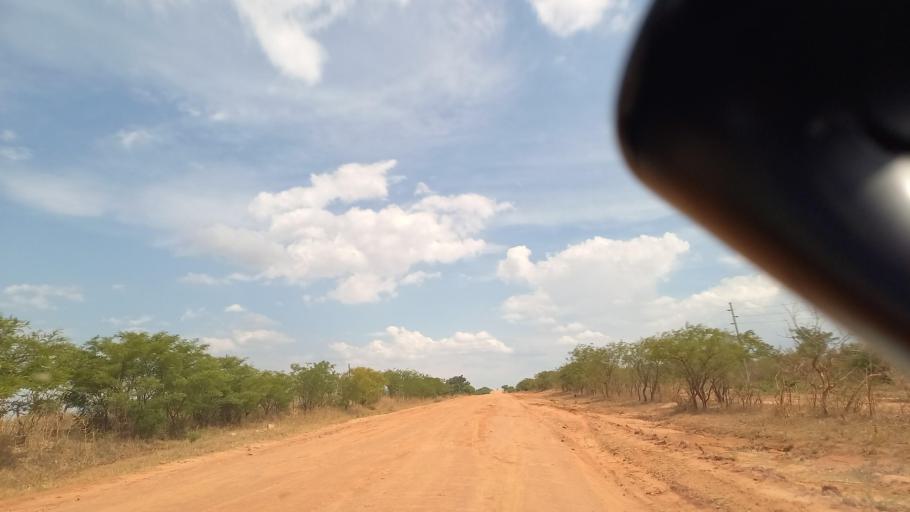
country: ZM
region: Lusaka
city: Kafue
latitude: -16.1234
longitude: 28.0421
